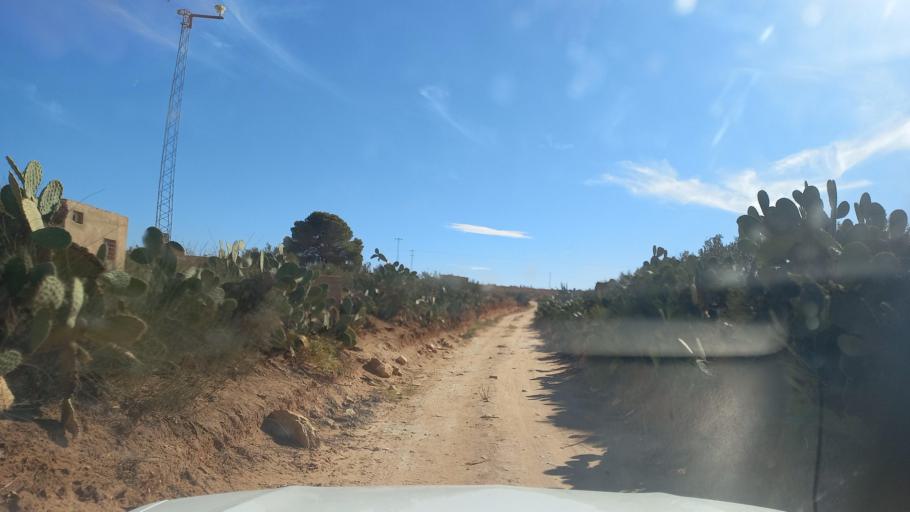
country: TN
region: Al Qasrayn
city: Kasserine
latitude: 35.2085
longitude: 8.9731
